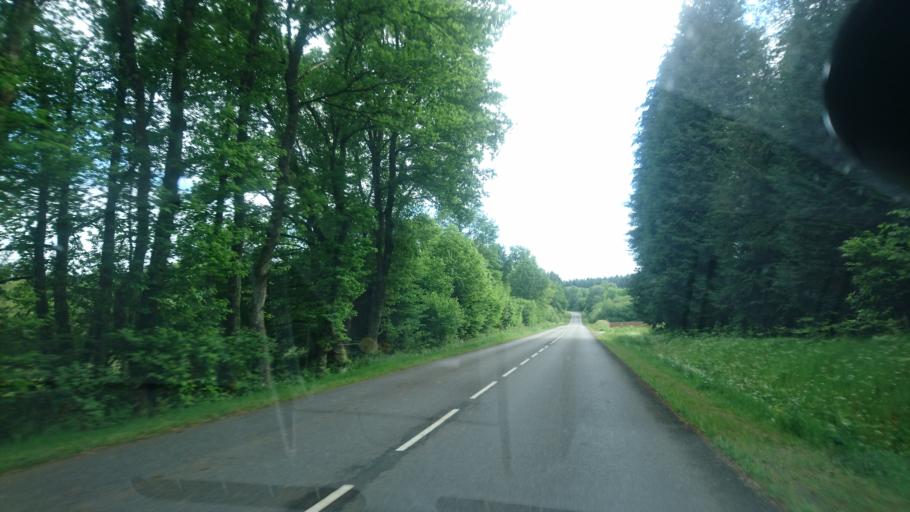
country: FR
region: Limousin
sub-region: Departement de la Haute-Vienne
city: Peyrat-le-Chateau
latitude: 45.7758
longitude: 1.7599
